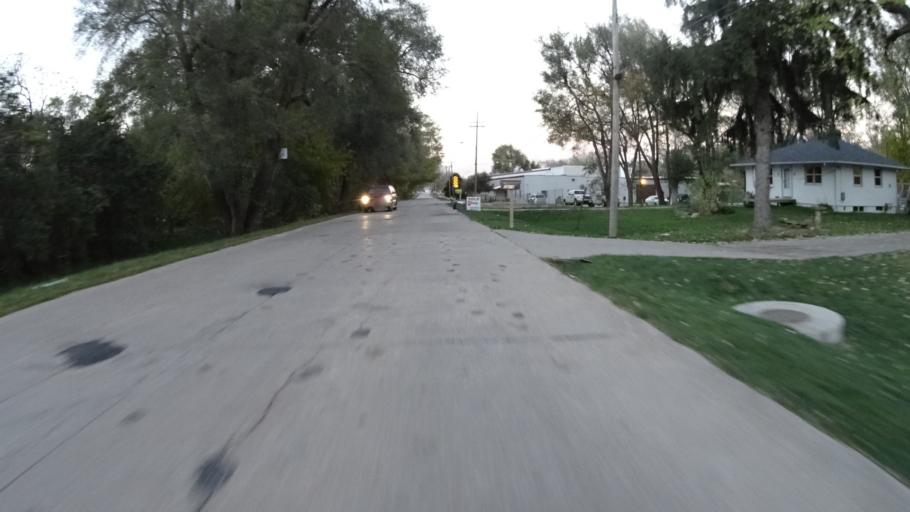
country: US
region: Nebraska
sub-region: Douglas County
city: Omaha
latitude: 41.1878
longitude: -95.9517
